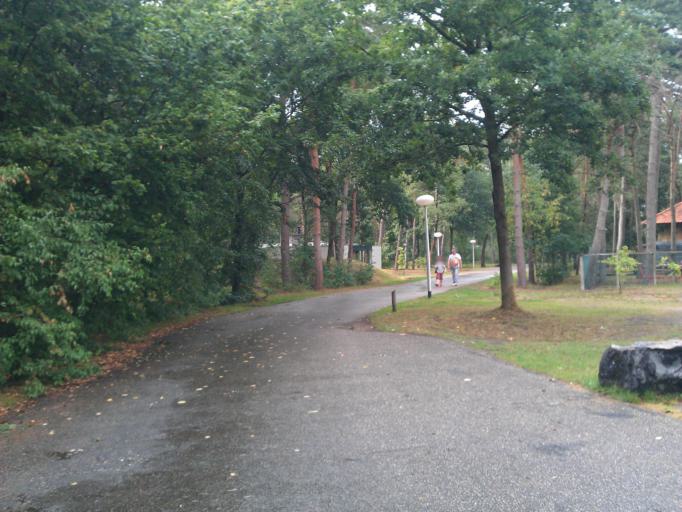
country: NL
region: North Brabant
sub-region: Gemeente Bladel en Netersel
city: Bladel
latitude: 51.3389
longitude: 5.2478
